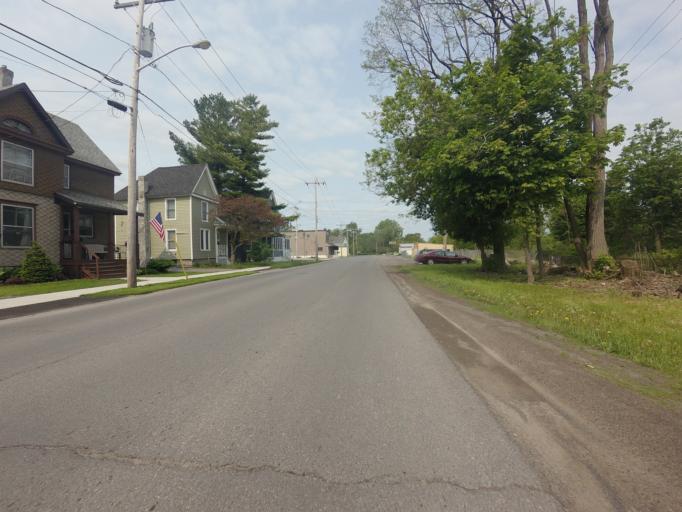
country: US
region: New York
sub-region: Jefferson County
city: Watertown
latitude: 43.9766
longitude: -75.8939
